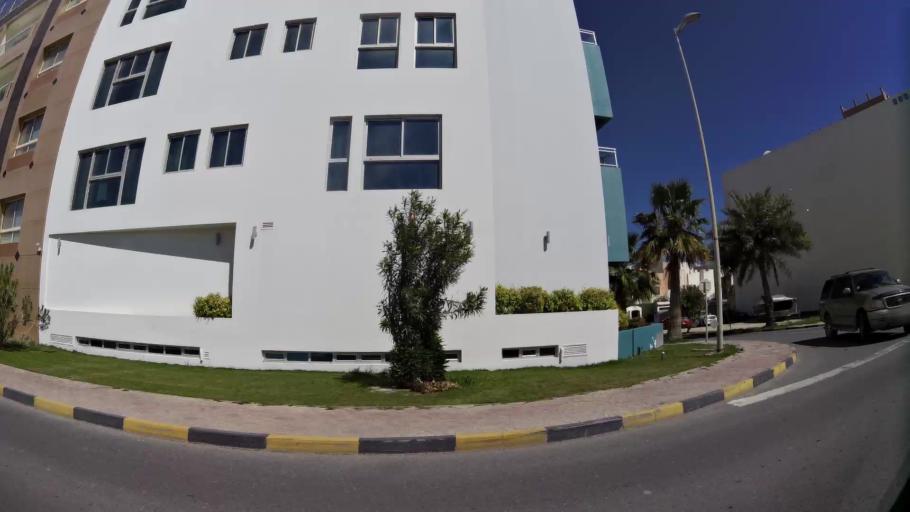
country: BH
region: Muharraq
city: Al Hadd
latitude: 26.2958
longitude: 50.6583
